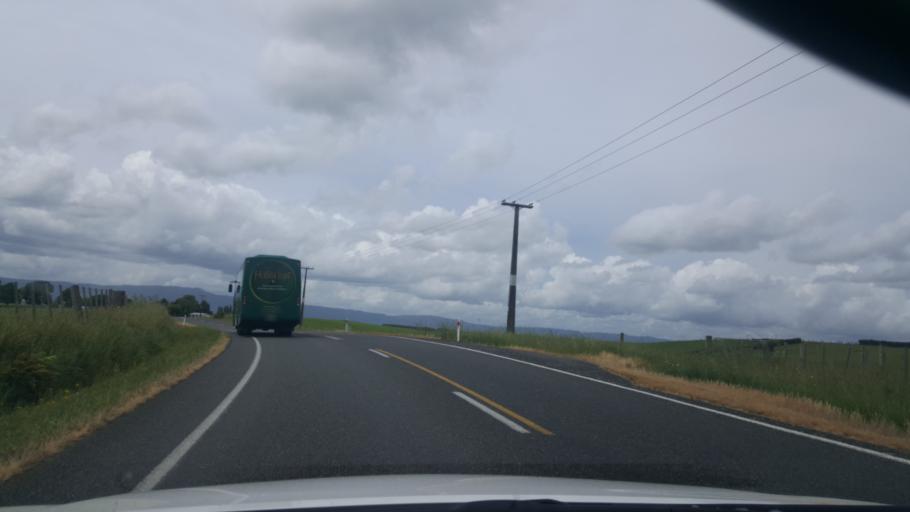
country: NZ
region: Waikato
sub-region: Matamata-Piako District
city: Matamata
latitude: -37.8778
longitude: 175.7150
